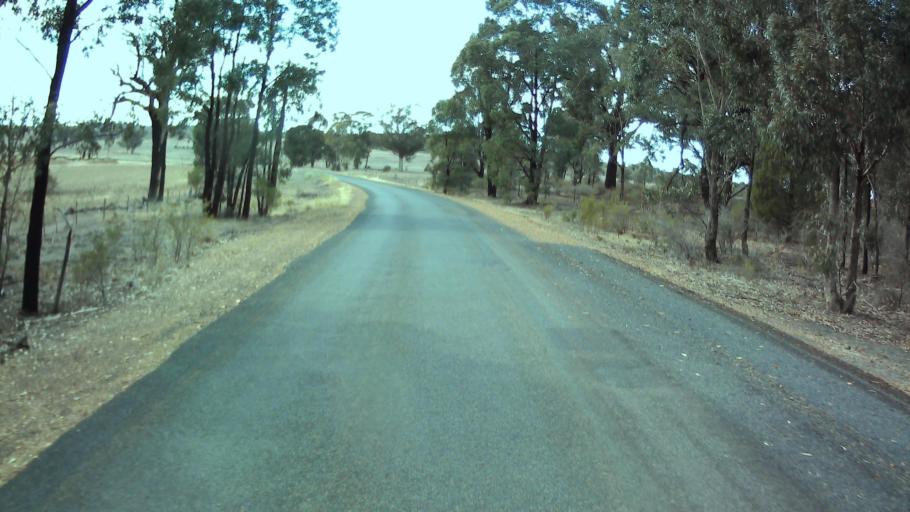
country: AU
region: New South Wales
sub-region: Weddin
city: Grenfell
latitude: -33.8444
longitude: 148.2422
